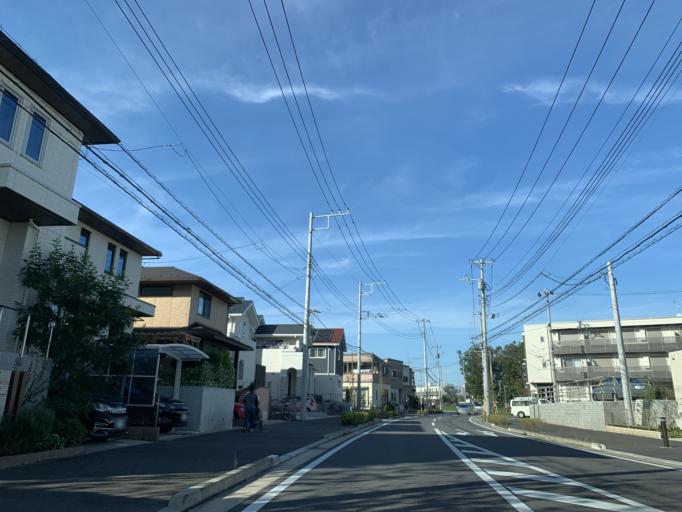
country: JP
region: Chiba
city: Nagareyama
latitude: 35.8775
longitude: 139.9269
